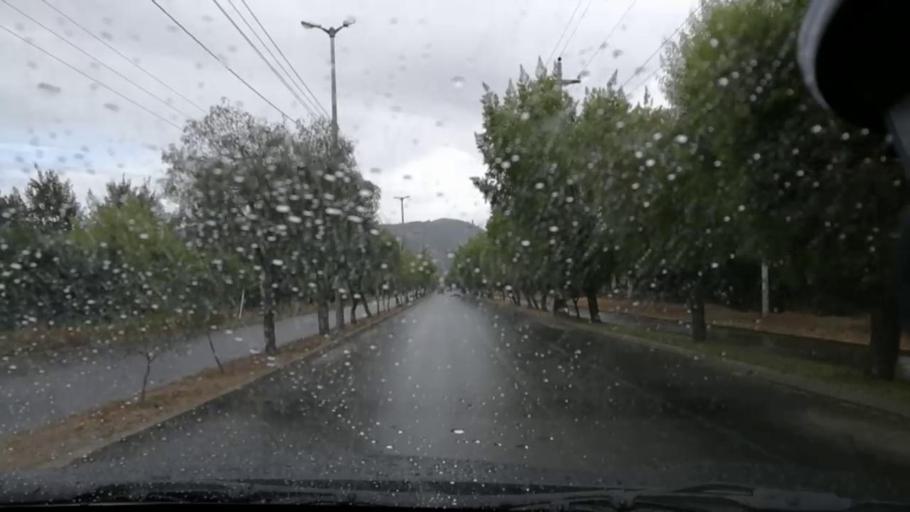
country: PE
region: Cajamarca
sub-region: Provincia de Cajamarca
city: Cajamarca
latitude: -7.1652
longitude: -78.4856
